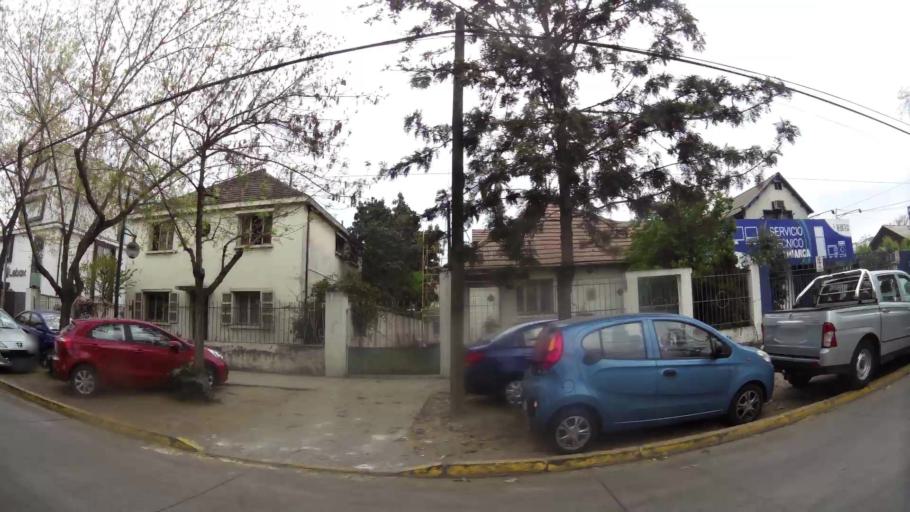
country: CL
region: Santiago Metropolitan
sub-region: Provincia de Santiago
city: Villa Presidente Frei, Nunoa, Santiago, Chile
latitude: -33.4662
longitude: -70.6003
